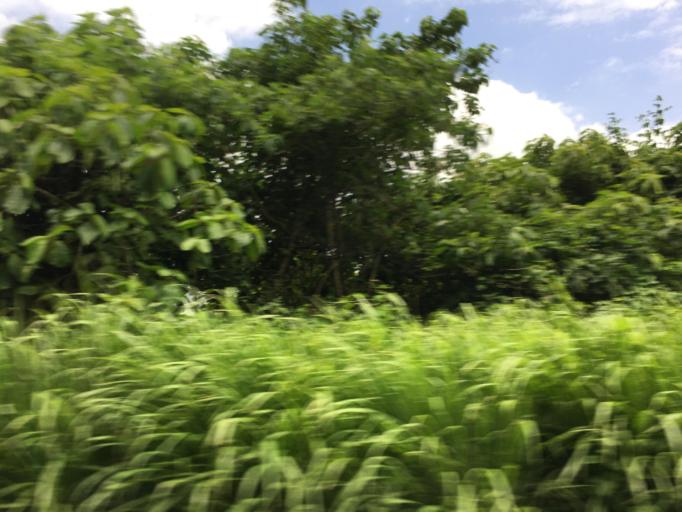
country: GT
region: Guatemala
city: Villa Canales
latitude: 14.4429
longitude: -90.5334
